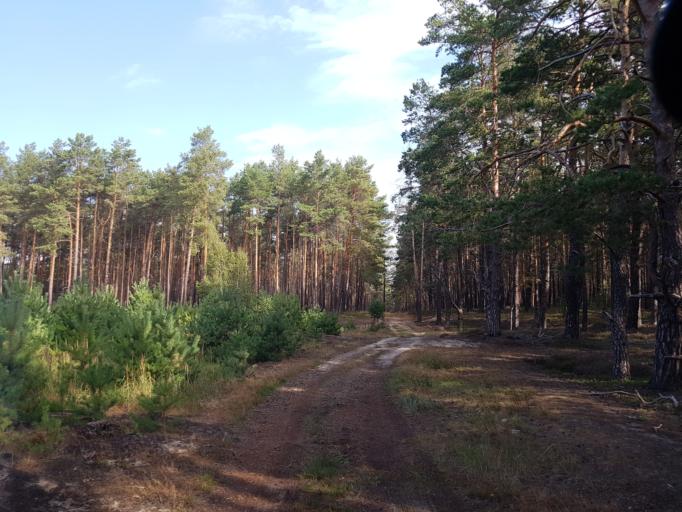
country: DE
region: Brandenburg
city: Finsterwalde
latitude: 51.5920
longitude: 13.7580
